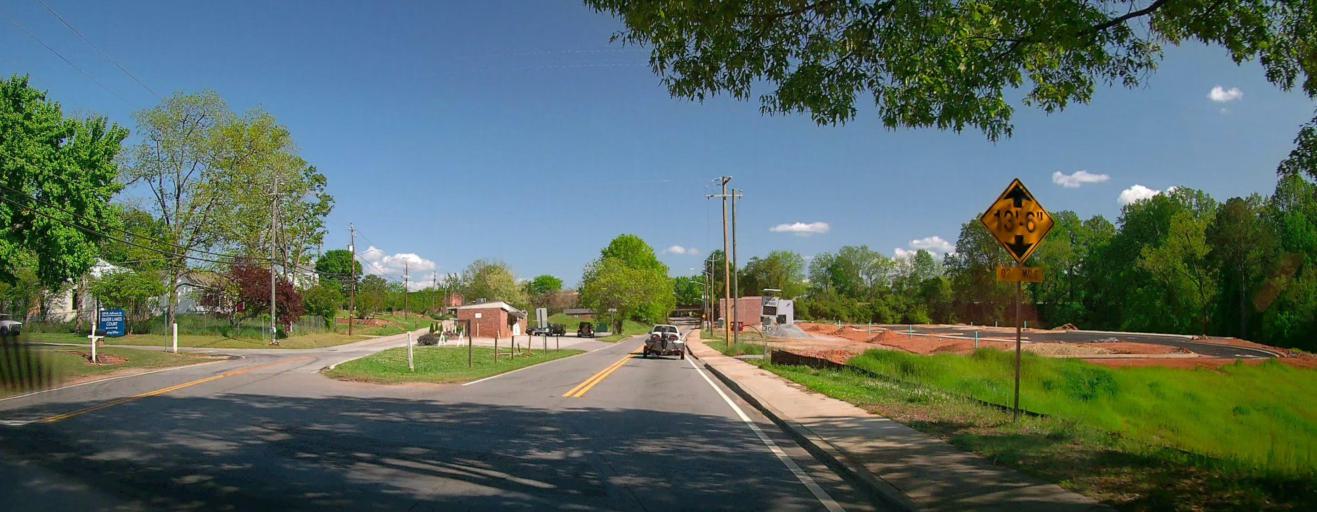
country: US
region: Georgia
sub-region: Morgan County
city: Madison
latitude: 33.5999
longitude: -83.4729
